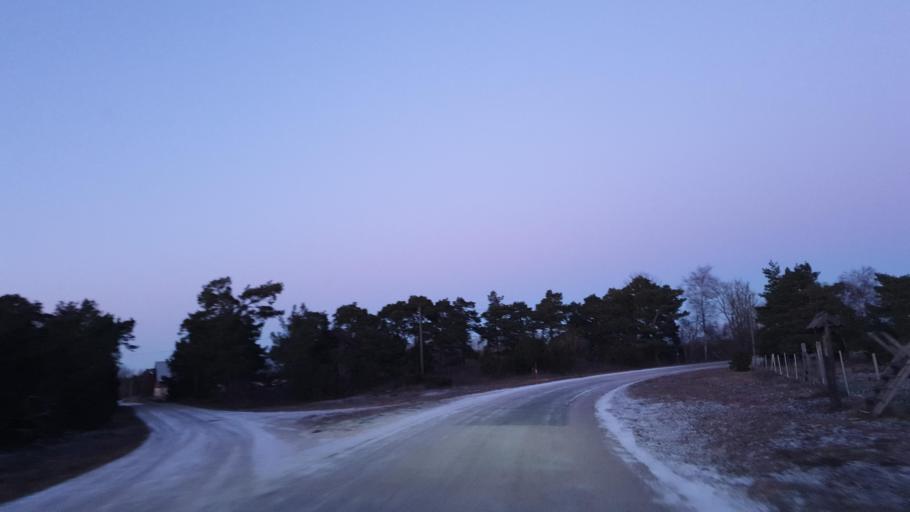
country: SE
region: Gotland
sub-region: Gotland
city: Slite
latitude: 57.4170
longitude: 18.8144
